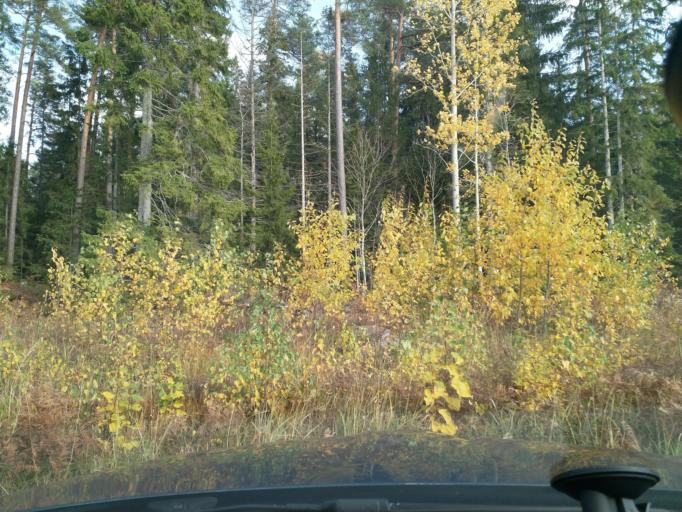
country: LV
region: Dundaga
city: Dundaga
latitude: 57.6226
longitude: 22.2781
